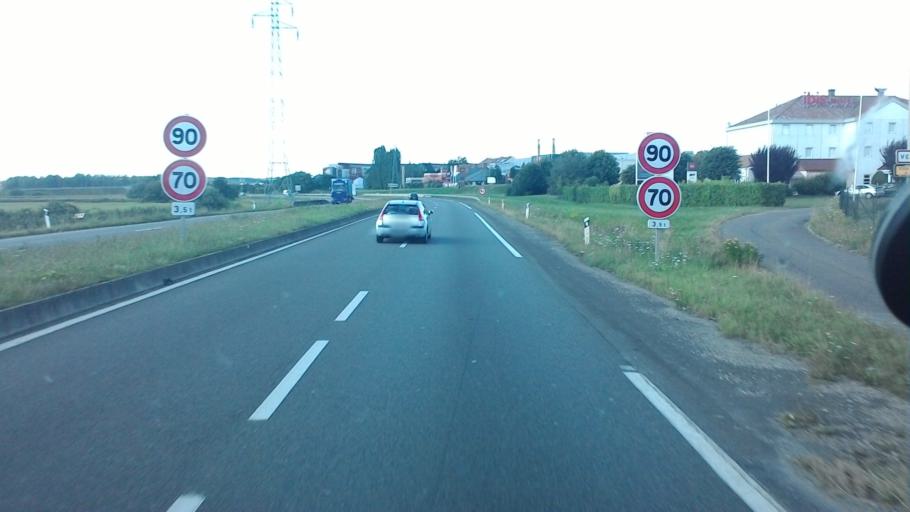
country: FR
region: Franche-Comte
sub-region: Departement de la Haute-Saone
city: Noidans-les-Vesoul
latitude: 47.6295
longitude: 6.1384
